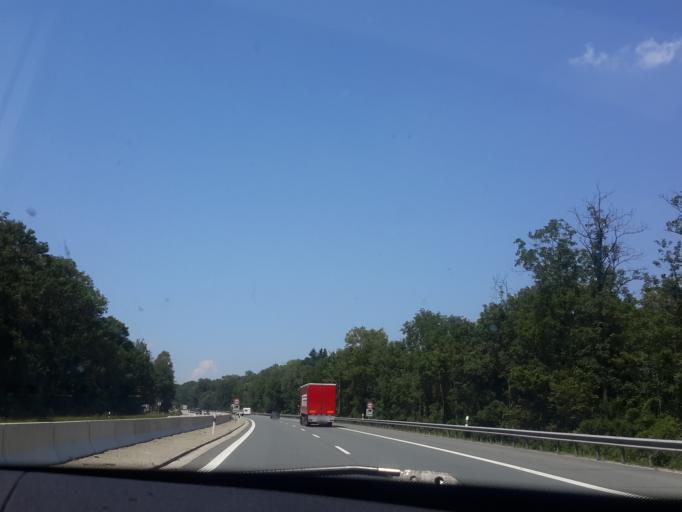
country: AT
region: Tyrol
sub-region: Politischer Bezirk Kufstein
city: Erl
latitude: 47.6985
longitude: 12.1614
